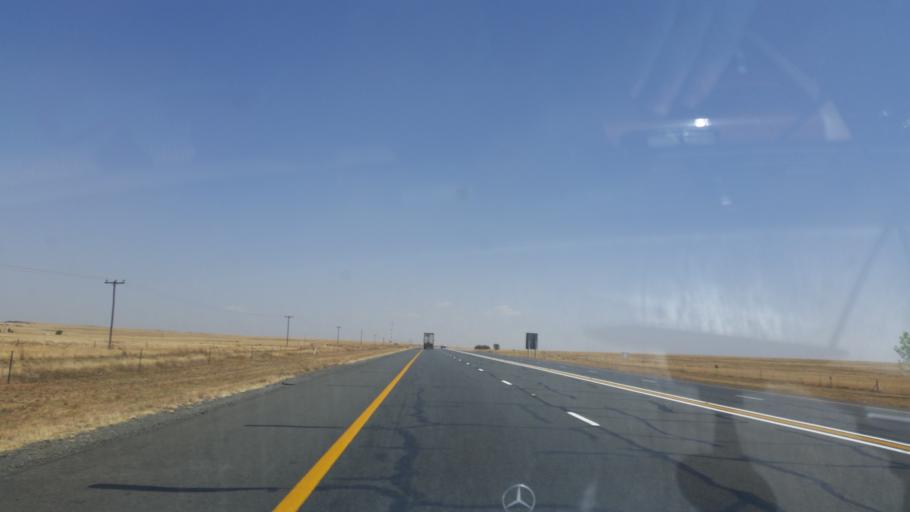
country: ZA
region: Orange Free State
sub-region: Lejweleputswa District Municipality
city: Brandfort
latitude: -28.8550
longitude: 26.5631
